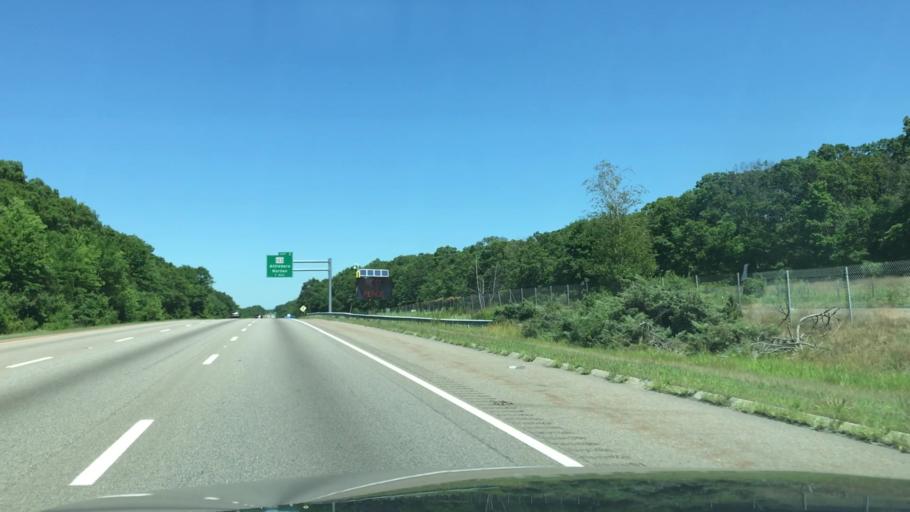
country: US
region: Massachusetts
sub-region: Bristol County
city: North Seekonk
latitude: 41.9175
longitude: -71.3321
